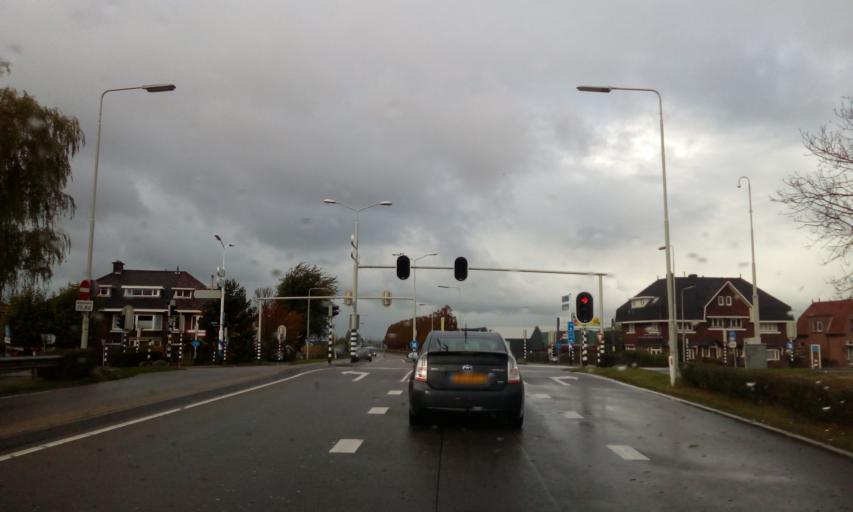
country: NL
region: South Holland
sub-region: Gemeente Westland
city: Honselersdijk
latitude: 52.0009
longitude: 4.2191
